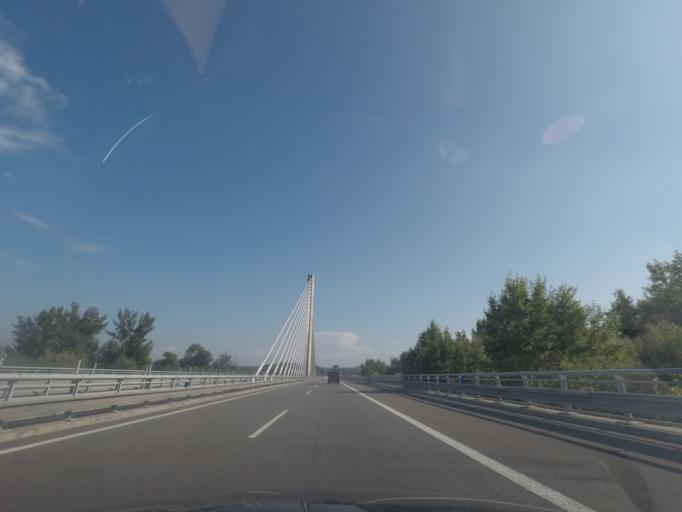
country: PL
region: Silesian Voivodeship
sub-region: Powiat raciborski
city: Chalupki
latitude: 49.8888
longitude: 18.3046
